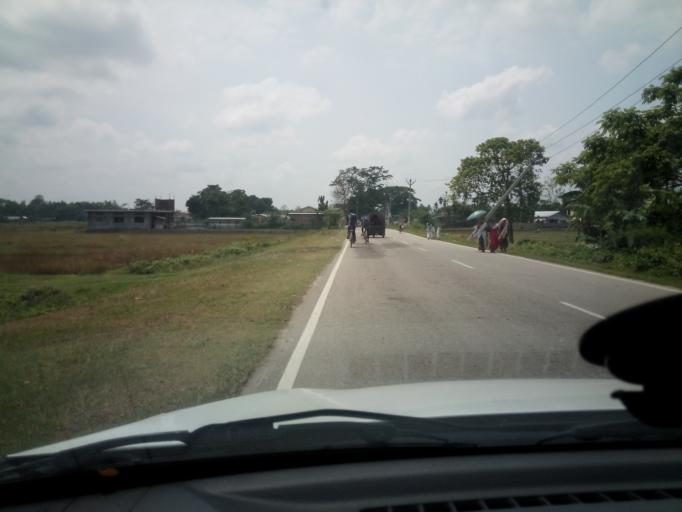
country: IN
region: Assam
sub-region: Udalguri
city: Udalguri
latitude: 26.7152
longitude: 92.2002
